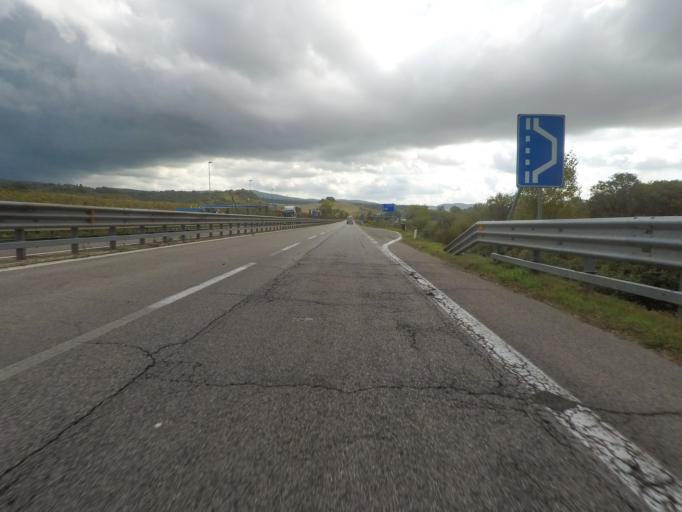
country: IT
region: Tuscany
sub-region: Provincia di Siena
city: Rapolano Terme
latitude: 43.3243
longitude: 11.5616
